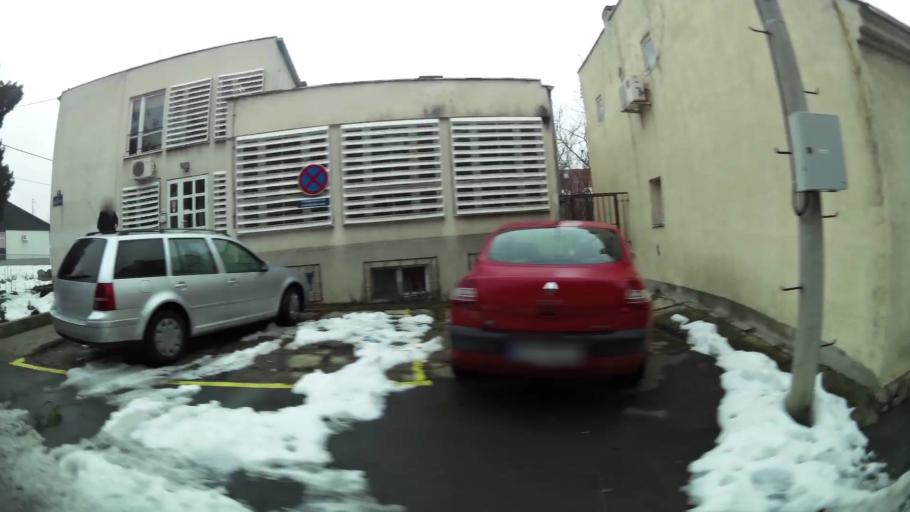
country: RS
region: Central Serbia
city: Belgrade
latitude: 44.7917
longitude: 20.4614
